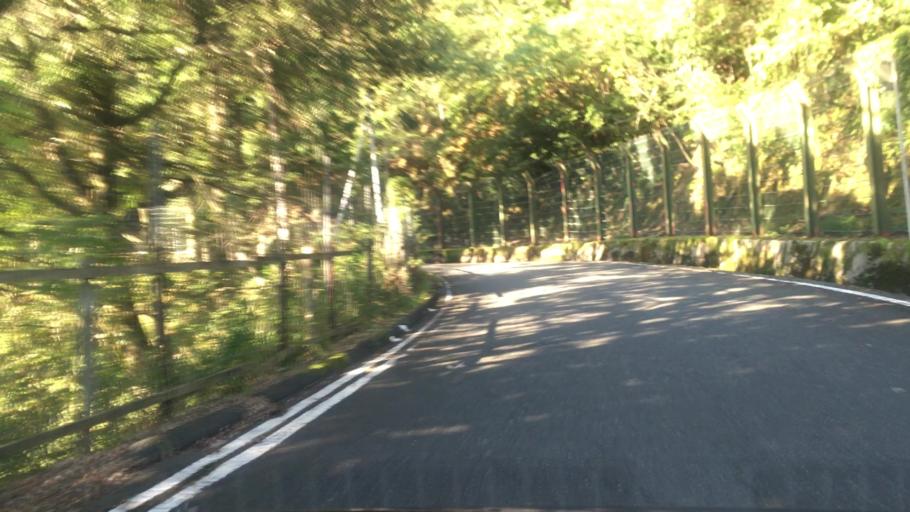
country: JP
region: Hyogo
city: Toyooka
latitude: 35.6145
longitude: 134.8785
